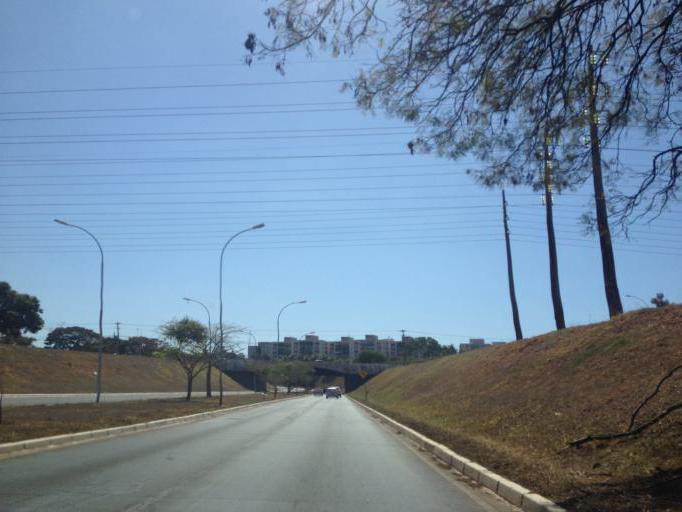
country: BR
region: Federal District
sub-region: Brasilia
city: Brasilia
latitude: -15.8121
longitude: -47.9380
